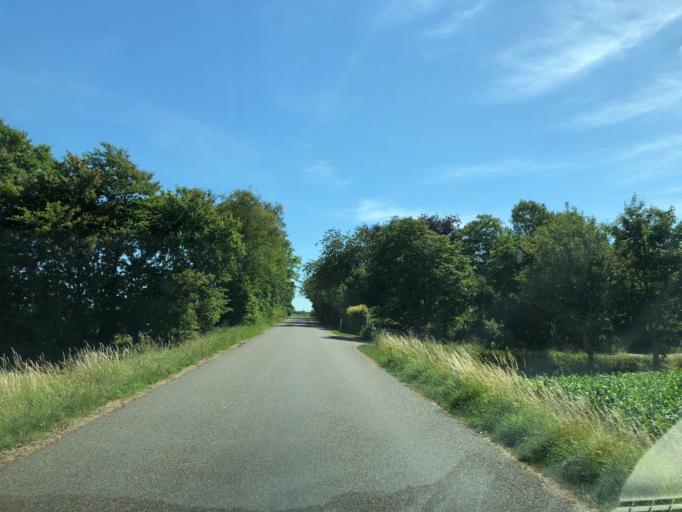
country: DK
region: Central Jutland
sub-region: Holstebro Kommune
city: Vinderup
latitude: 56.4065
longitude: 8.9093
